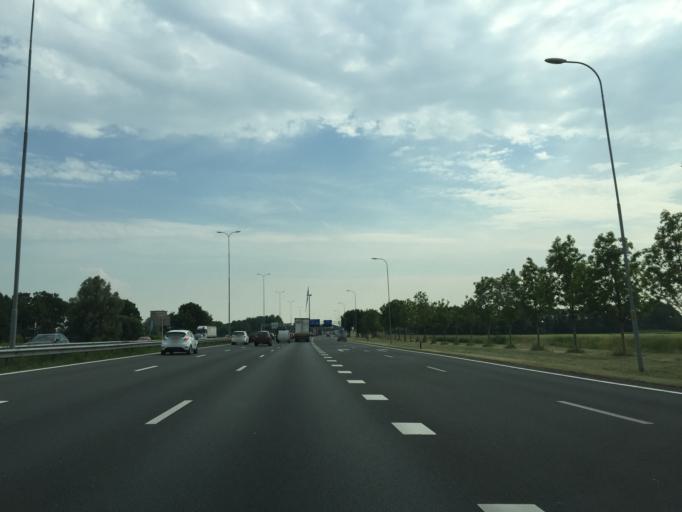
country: NL
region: Utrecht
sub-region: Gemeente Utrecht
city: Lunetten
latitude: 52.0385
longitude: 5.1391
